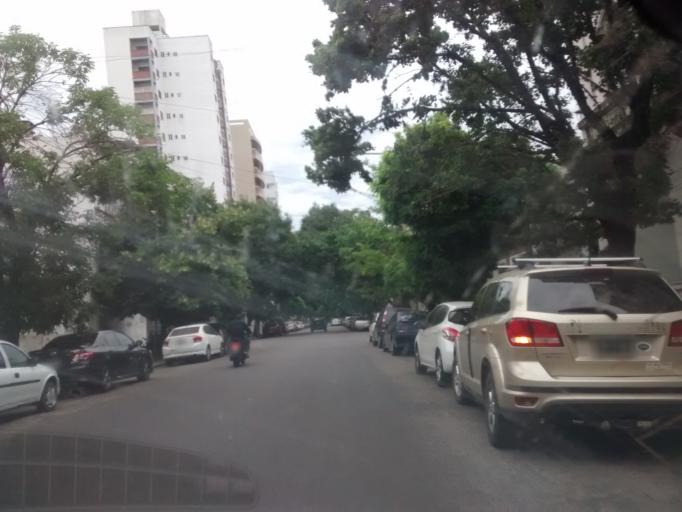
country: AR
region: Buenos Aires
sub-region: Partido de La Plata
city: La Plata
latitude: -34.9234
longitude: -57.9465
